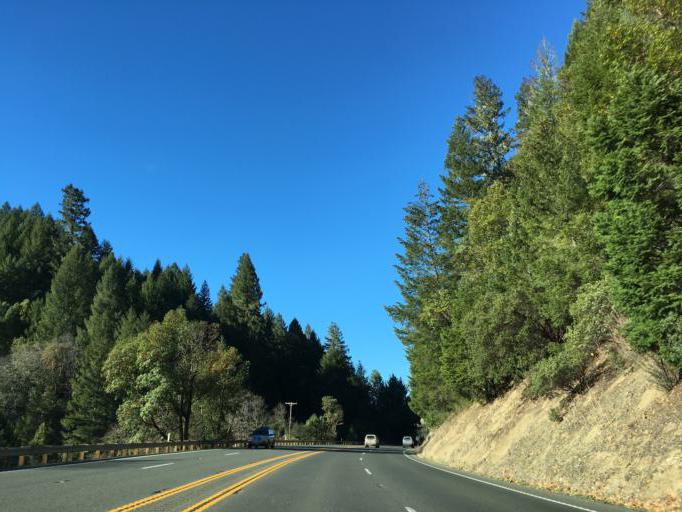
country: US
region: California
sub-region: Mendocino County
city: Brooktrails
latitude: 39.5146
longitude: -123.3895
